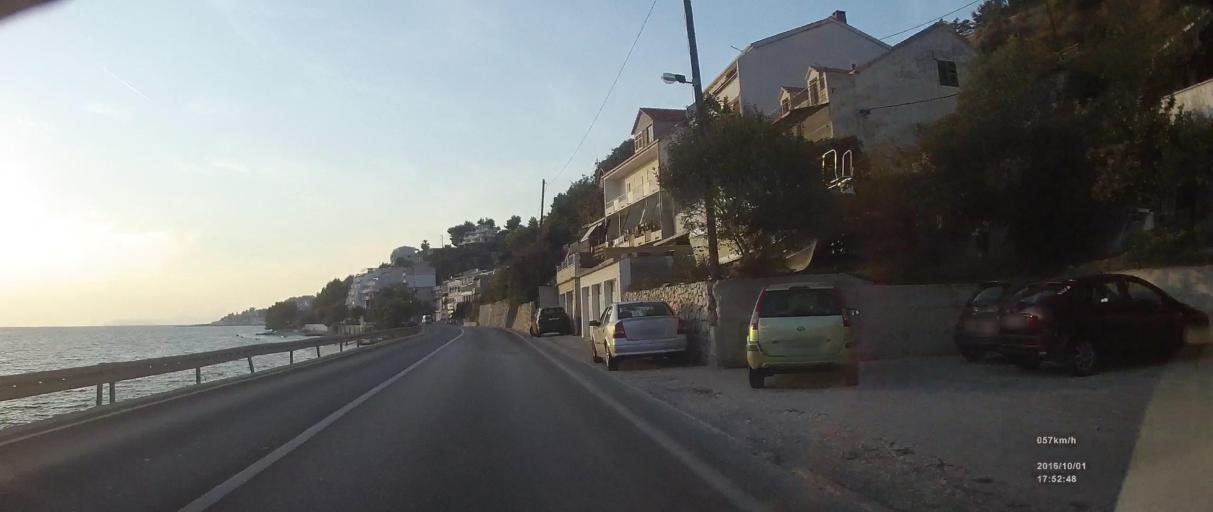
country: HR
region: Splitsko-Dalmatinska
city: Jesenice
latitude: 43.4556
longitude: 16.6167
